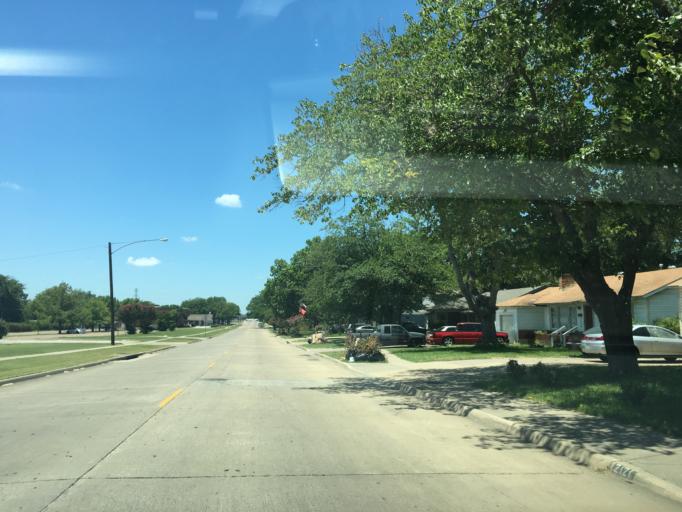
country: US
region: Texas
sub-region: Dallas County
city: Garland
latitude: 32.8507
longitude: -96.6742
